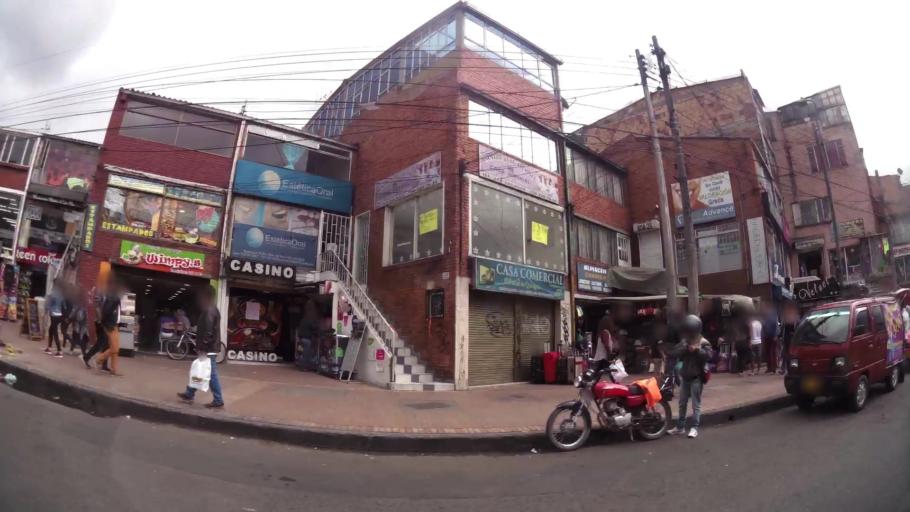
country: CO
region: Bogota D.C.
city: Barrio San Luis
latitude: 4.7069
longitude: -74.1070
